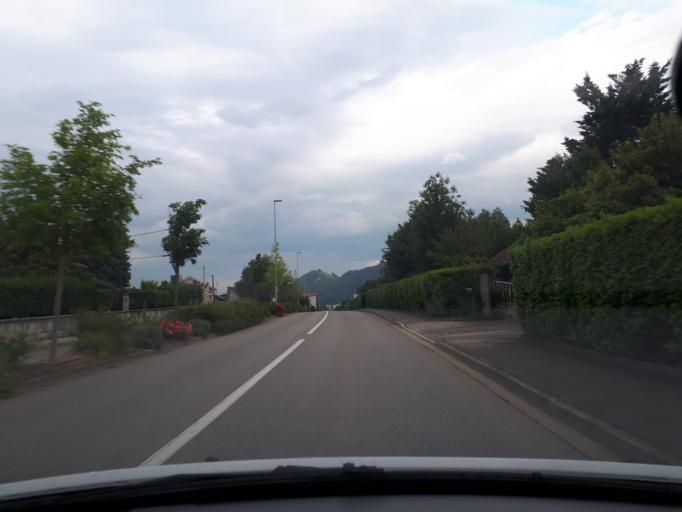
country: FR
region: Rhone-Alpes
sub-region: Departement de l'Isere
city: Eybens
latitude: 45.1507
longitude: 5.7454
